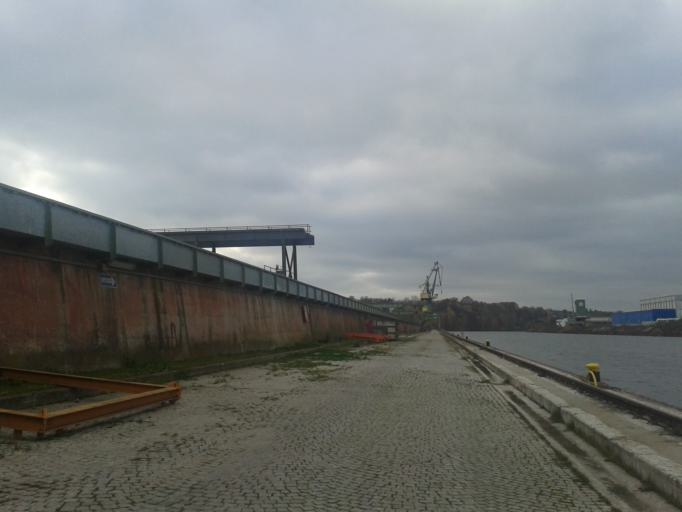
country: DE
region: Bavaria
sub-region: Upper Franconia
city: Hallstadt
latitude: 49.9103
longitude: 10.8641
